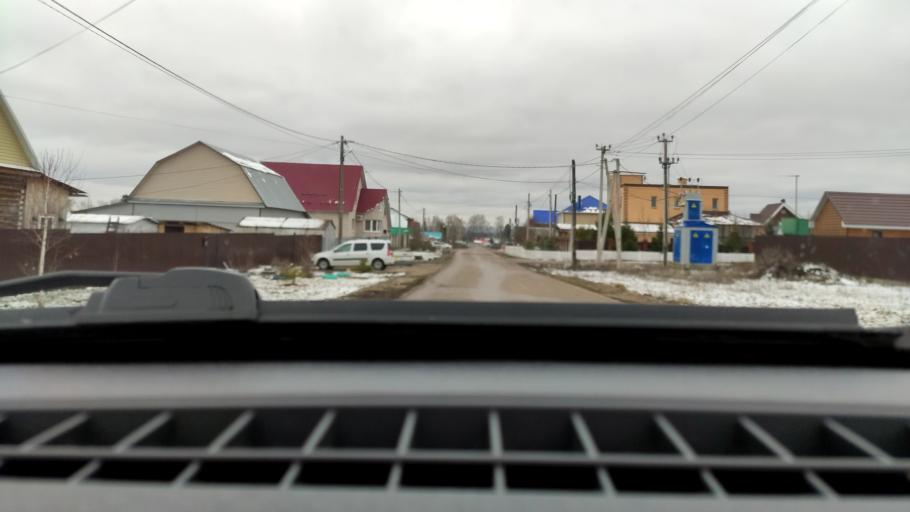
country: RU
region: Bashkortostan
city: Mikhaylovka
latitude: 54.8111
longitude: 55.8014
